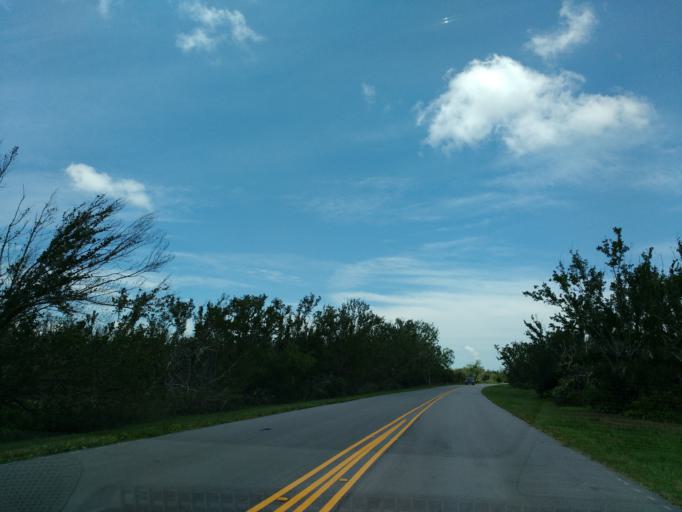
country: US
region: Florida
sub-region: Monroe County
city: Islamorada
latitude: 25.1395
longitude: -80.9300
